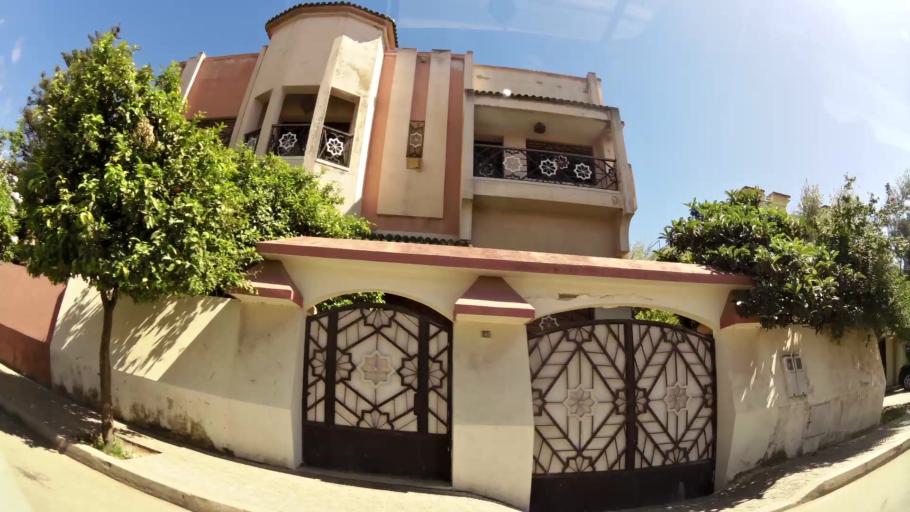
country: MA
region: Fes-Boulemane
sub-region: Fes
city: Fes
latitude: 34.0166
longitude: -4.9921
